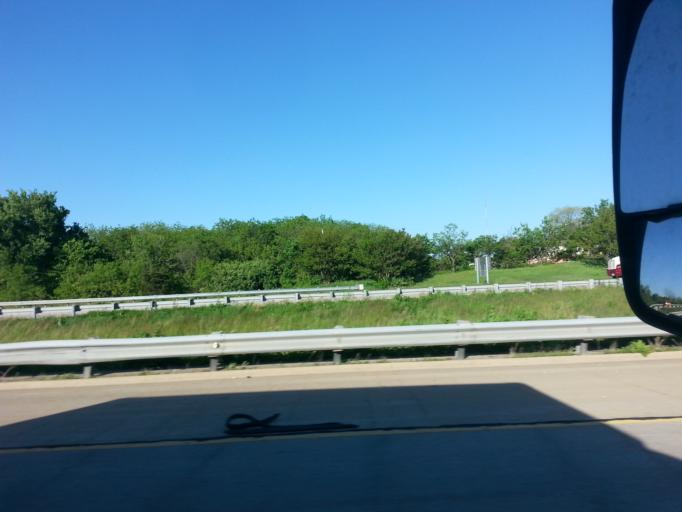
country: US
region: Illinois
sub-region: McLean County
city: Bloomington
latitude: 40.4507
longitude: -89.0233
